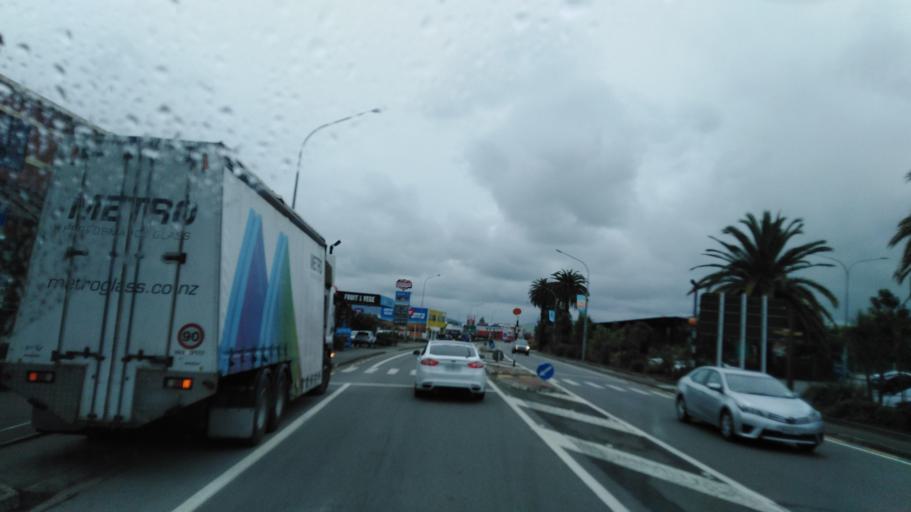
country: NZ
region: Marlborough
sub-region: Marlborough District
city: Blenheim
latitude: -41.5103
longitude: 173.9593
